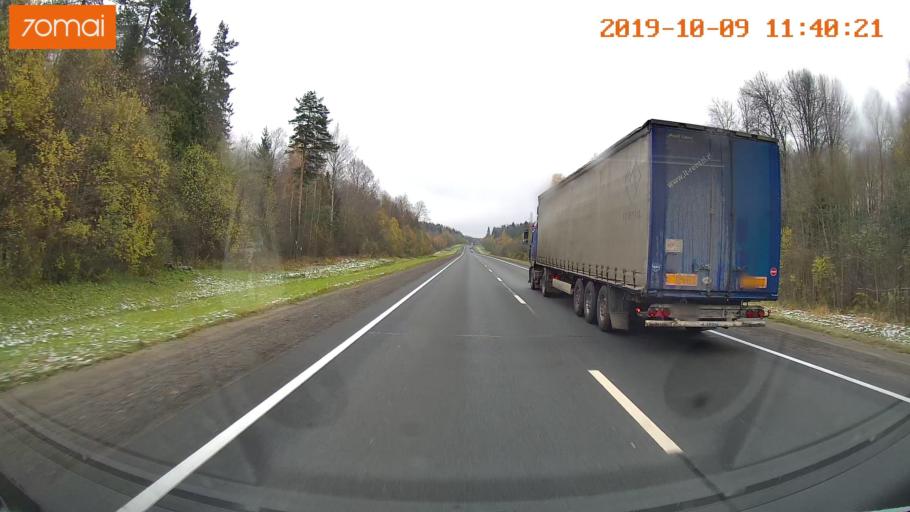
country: RU
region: Vologda
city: Gryazovets
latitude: 58.9436
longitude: 40.1738
